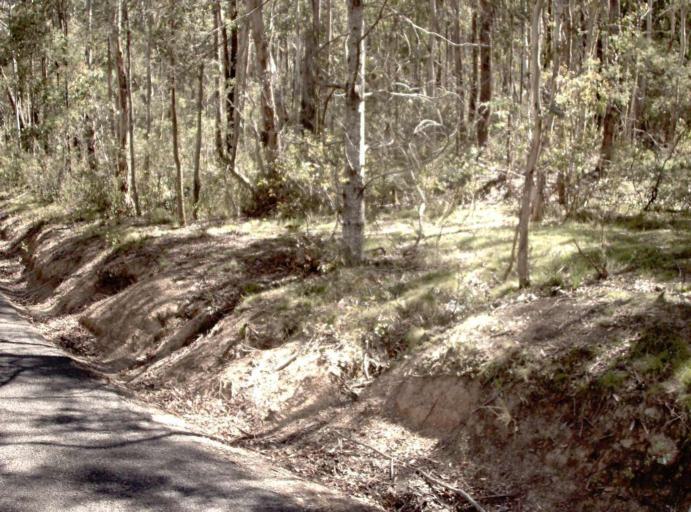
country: AU
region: New South Wales
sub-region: Bombala
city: Bombala
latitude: -37.1461
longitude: 148.7235
